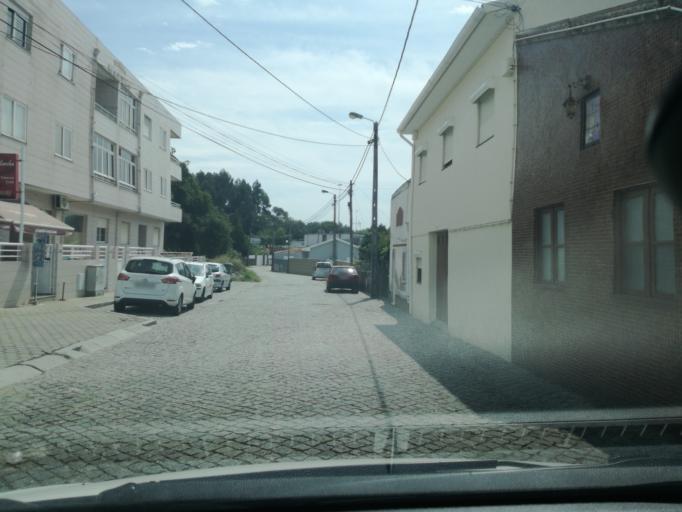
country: PT
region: Porto
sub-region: Vila Nova de Gaia
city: Grijo
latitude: 41.0179
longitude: -8.5852
